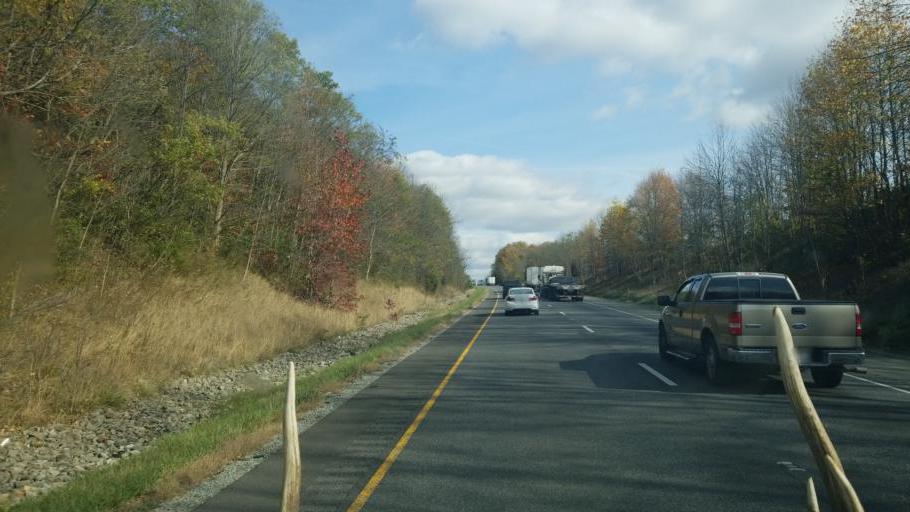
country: US
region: Indiana
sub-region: Henry County
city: New Castle
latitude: 39.8526
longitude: -85.4374
